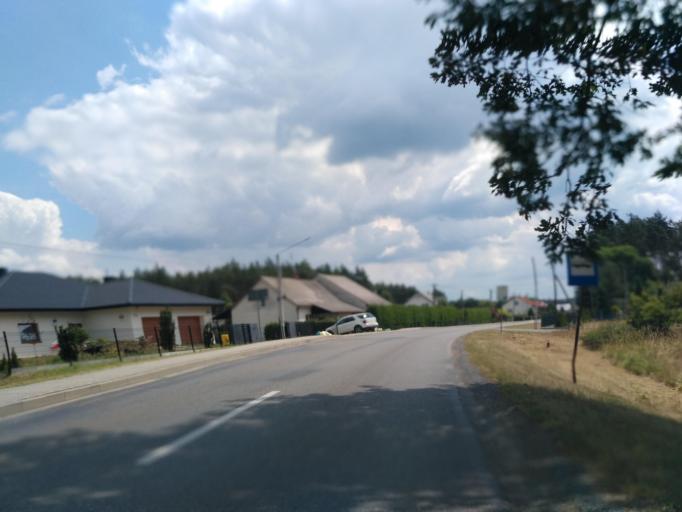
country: PL
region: Subcarpathian Voivodeship
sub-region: Powiat debicki
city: Czarna
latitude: 50.0312
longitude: 21.2902
